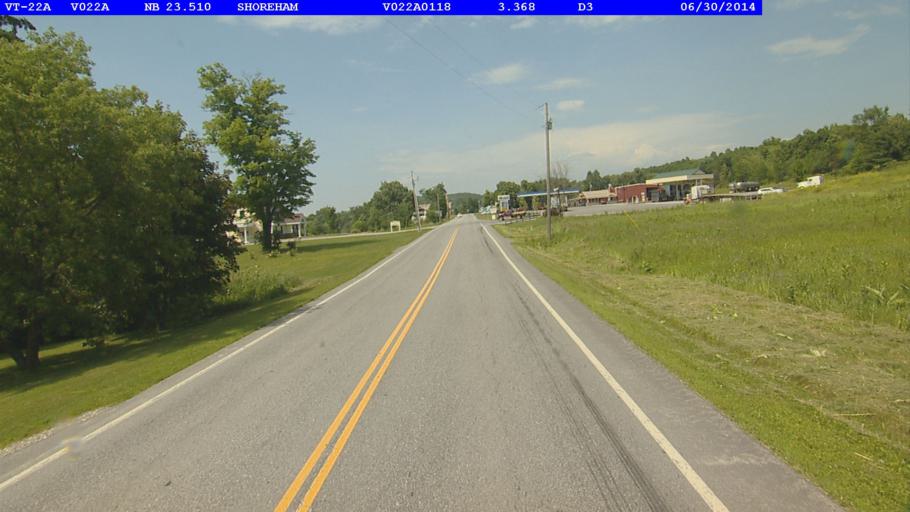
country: US
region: New York
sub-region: Essex County
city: Ticonderoga
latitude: 43.8981
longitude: -73.3085
